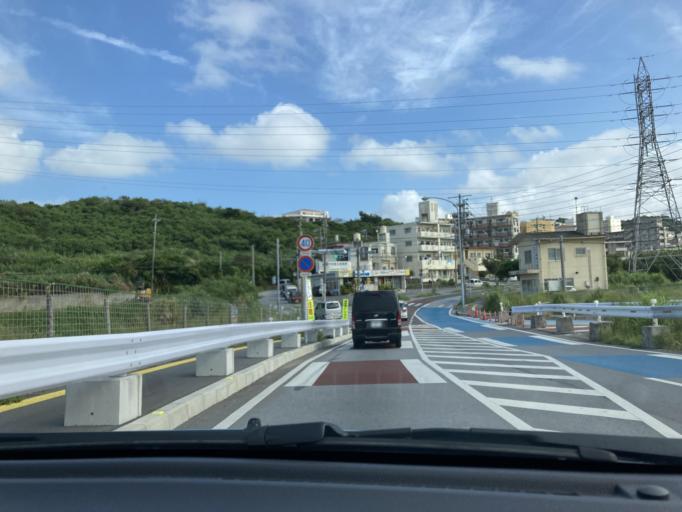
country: JP
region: Okinawa
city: Ginowan
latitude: 26.2396
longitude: 127.7490
